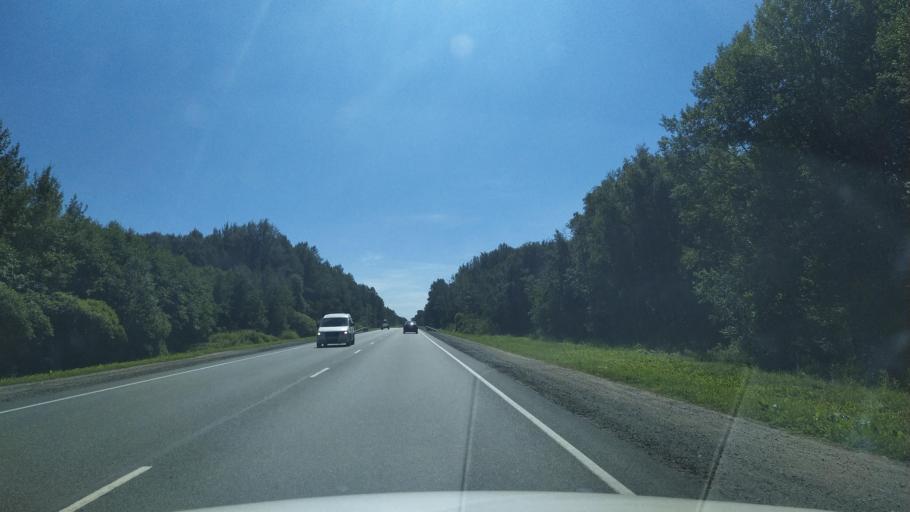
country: RU
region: Pskov
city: Pskov
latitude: 57.7764
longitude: 28.4000
